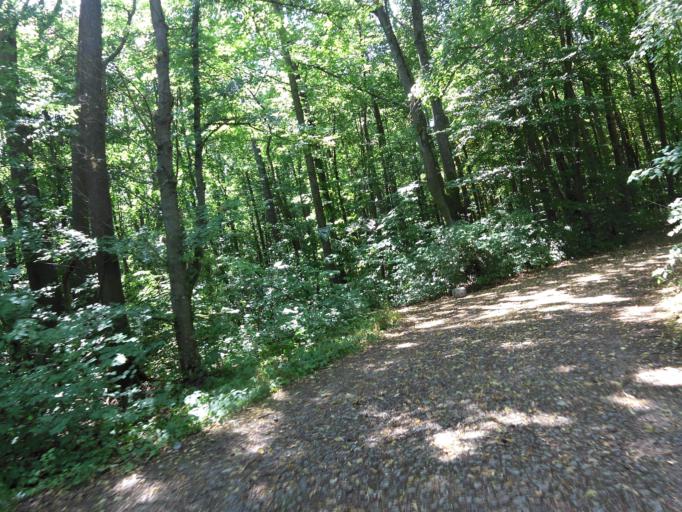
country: DE
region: Bavaria
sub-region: Regierungsbezirk Unterfranken
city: Hochberg
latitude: 49.7790
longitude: 9.9099
